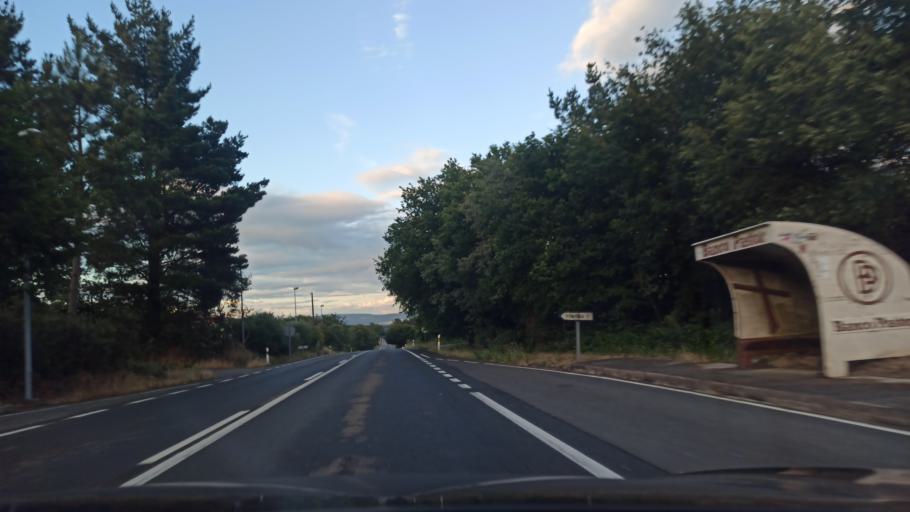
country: ES
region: Galicia
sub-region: Provincia de Pontevedra
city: Rodeiro
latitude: 42.7736
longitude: -7.9564
